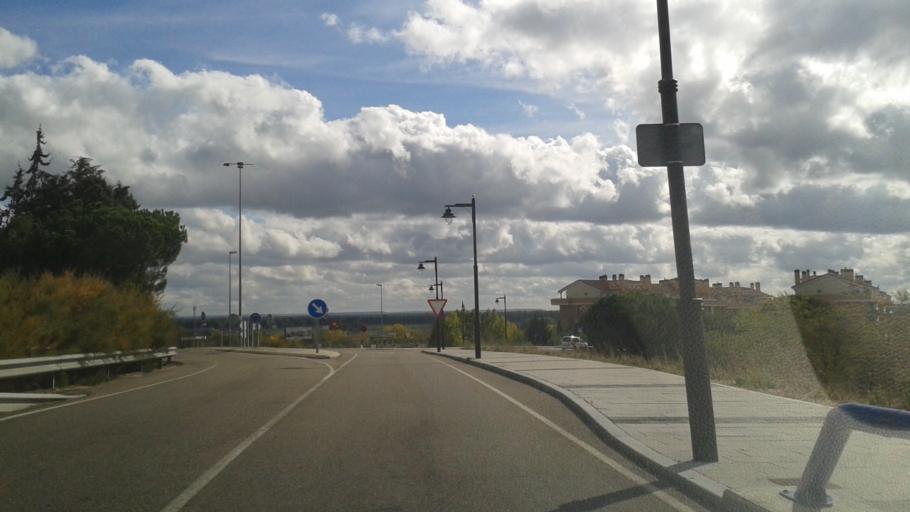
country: ES
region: Castille and Leon
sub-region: Provincia de Valladolid
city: Arroyo
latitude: 41.6124
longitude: -4.7952
